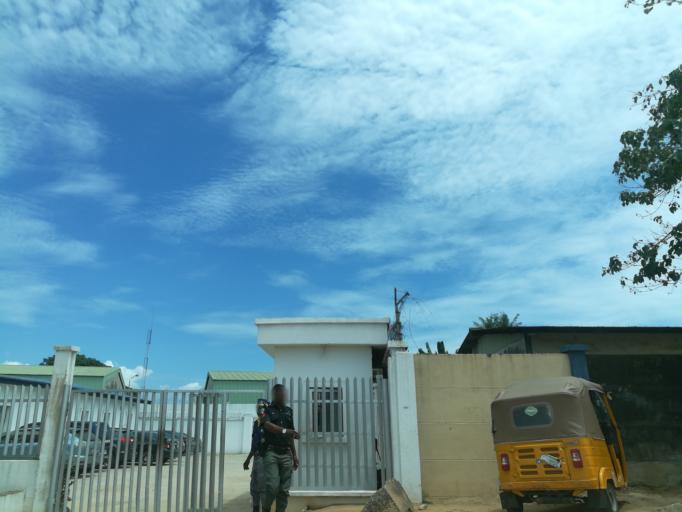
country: NG
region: Lagos
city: Ebute Ikorodu
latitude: 6.5700
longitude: 3.4820
